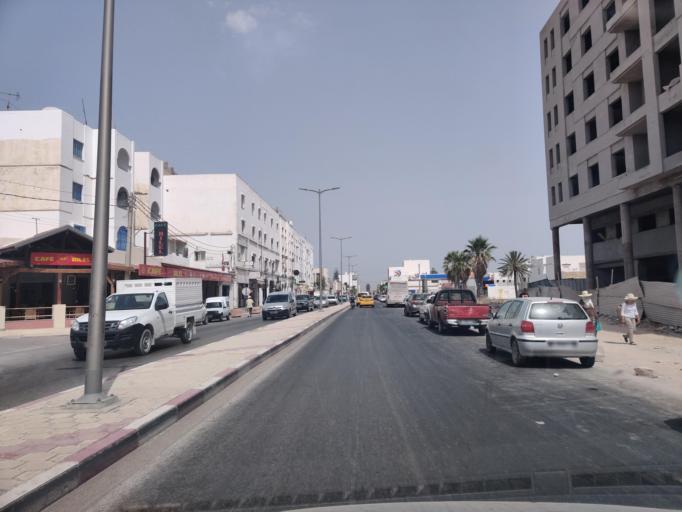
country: TN
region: Nabul
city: Bu `Urqub
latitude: 36.5944
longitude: 10.5019
